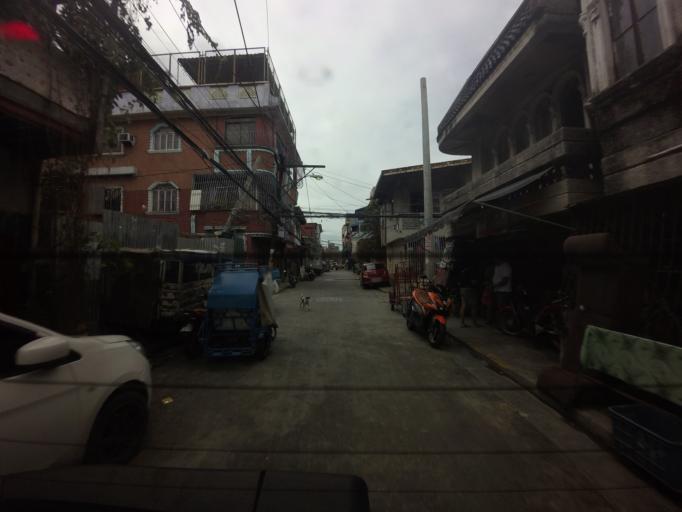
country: PH
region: Metro Manila
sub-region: City of Manila
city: Manila
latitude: 14.6084
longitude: 120.9642
